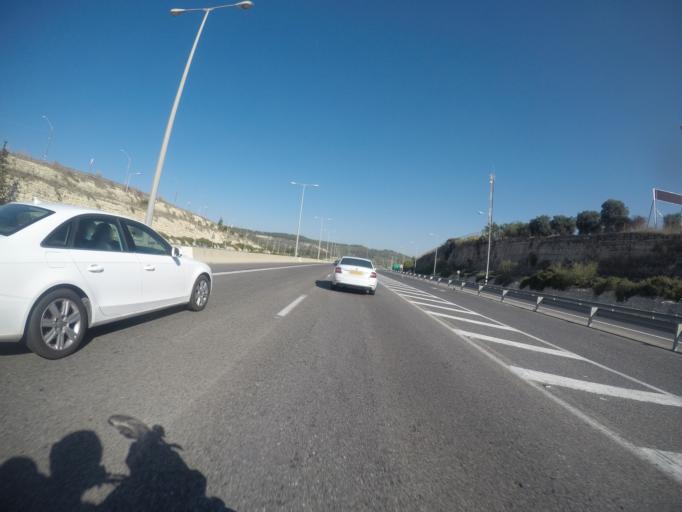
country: IL
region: Haifa
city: Daliyat el Karmil
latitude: 32.6324
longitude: 35.0637
